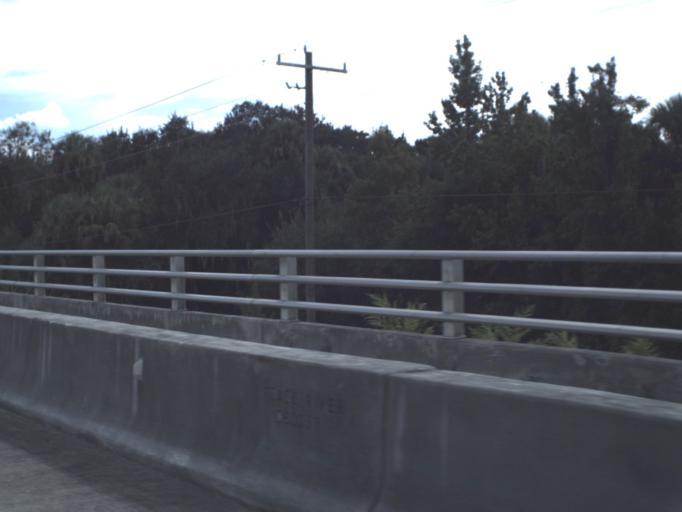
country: US
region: Florida
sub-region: Hardee County
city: Zolfo Springs
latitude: 27.5048
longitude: -81.8008
